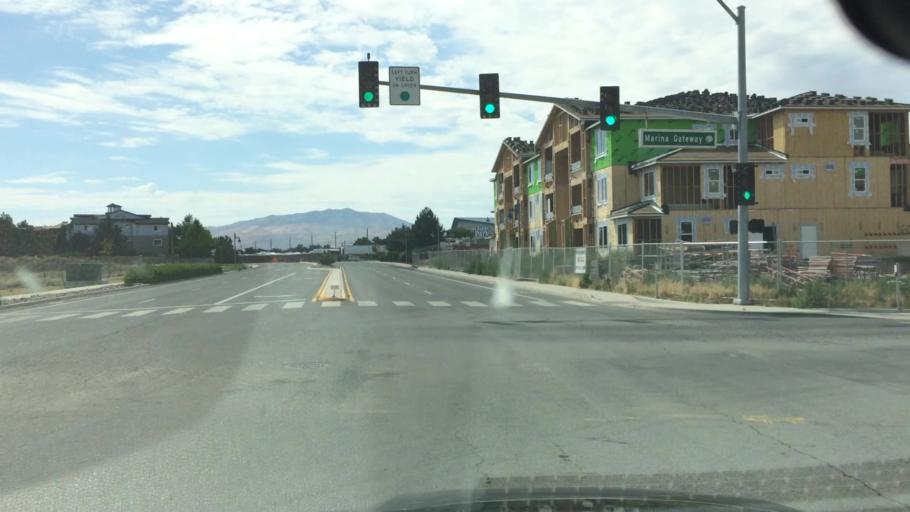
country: US
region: Nevada
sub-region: Washoe County
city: Sparks
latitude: 39.5368
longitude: -119.7224
